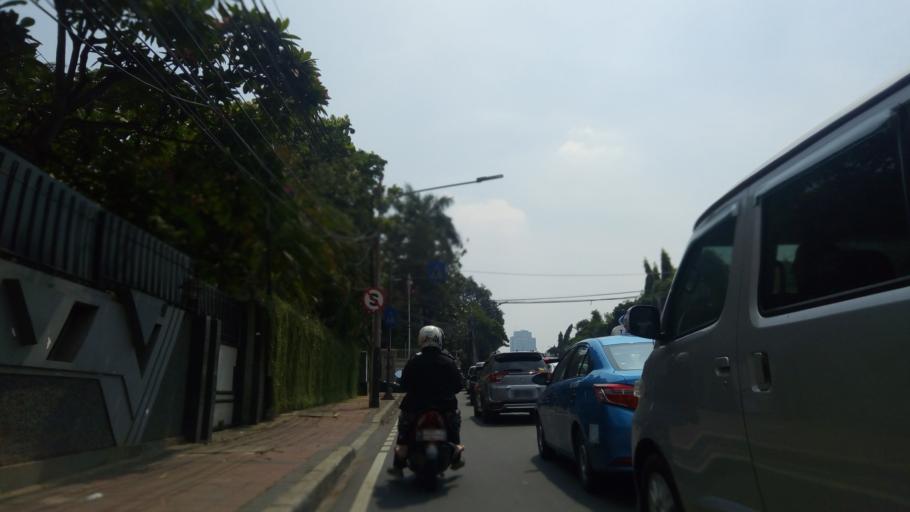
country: ID
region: Jakarta Raya
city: Jakarta
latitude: -6.2012
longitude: 106.8280
